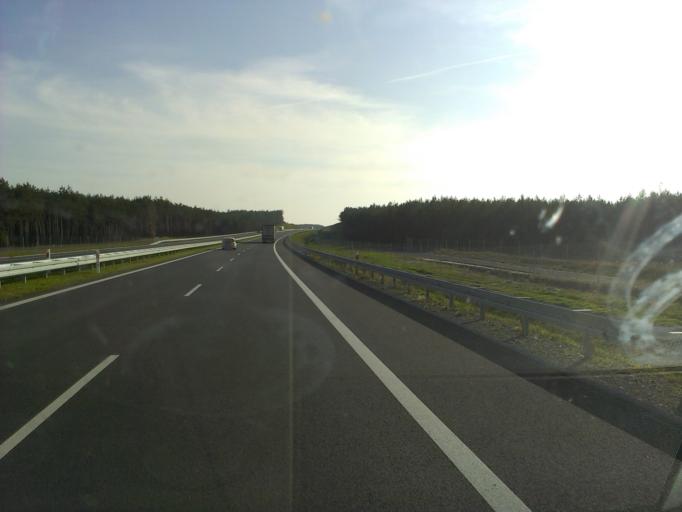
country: PL
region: Lubusz
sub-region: Powiat miedzyrzecki
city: Skwierzyna
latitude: 52.6084
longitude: 15.4162
